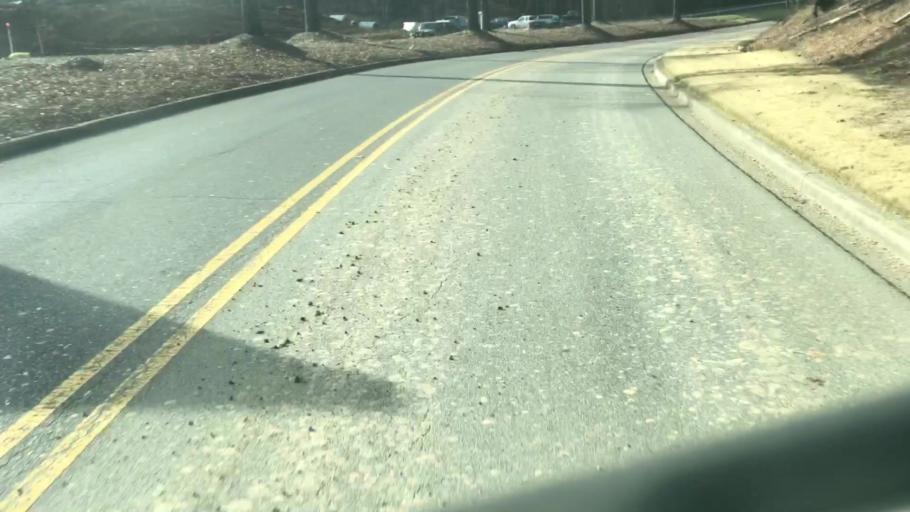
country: US
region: Alabama
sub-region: Jefferson County
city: Cahaba Heights
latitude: 33.4745
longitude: -86.7018
